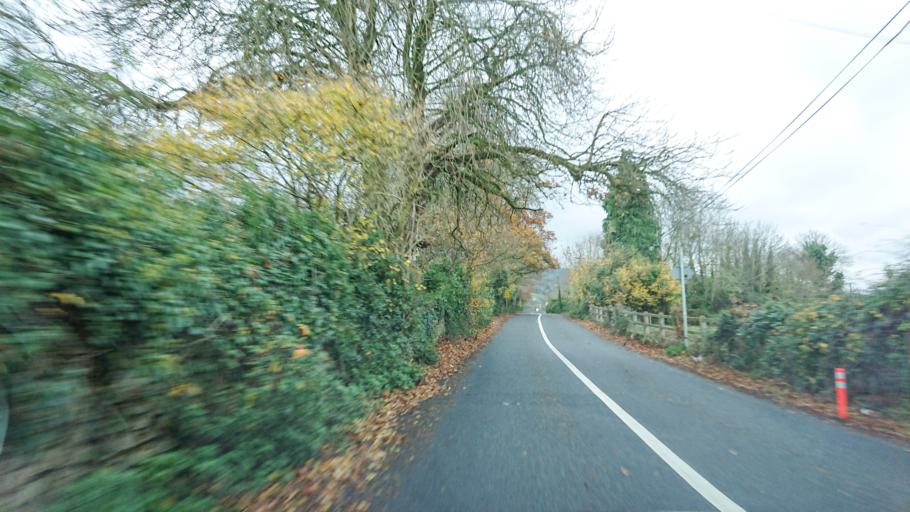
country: IE
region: Munster
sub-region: South Tipperary
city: Cluain Meala
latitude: 52.3548
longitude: -7.6710
